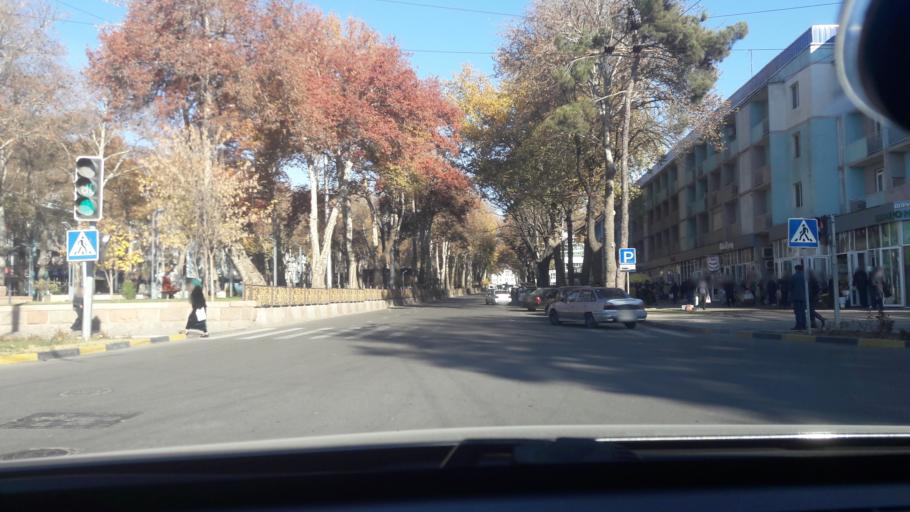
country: TJ
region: Dushanbe
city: Dushanbe
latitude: 38.5583
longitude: 68.7998
